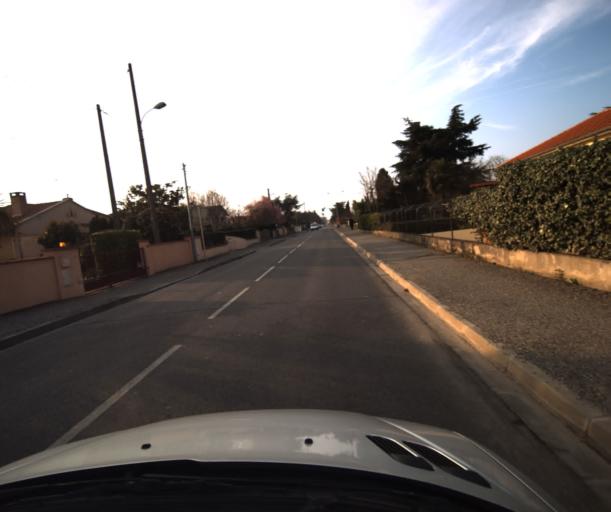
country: FR
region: Midi-Pyrenees
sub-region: Departement de la Haute-Garonne
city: Castelginest
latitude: 43.6874
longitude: 1.4374
